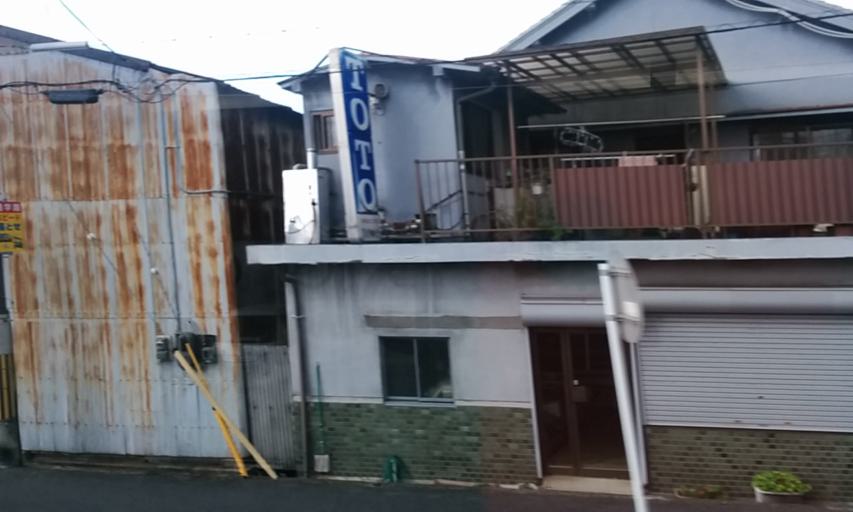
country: JP
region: Nara
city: Tawaramoto
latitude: 34.5550
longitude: 135.7902
